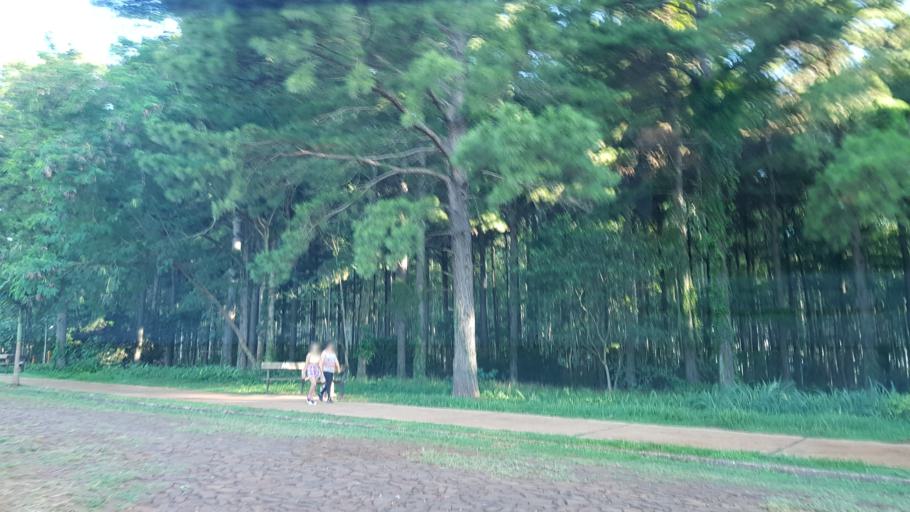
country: AR
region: Misiones
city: Puerto Libertad
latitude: -25.9248
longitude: -54.5858
